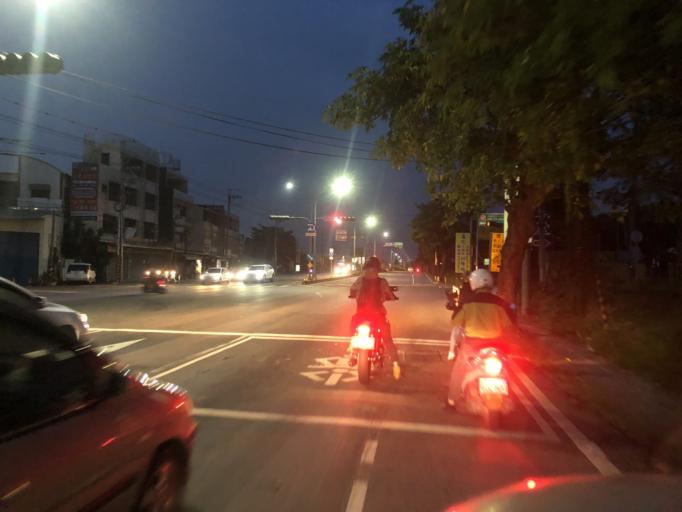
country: TW
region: Taiwan
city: Yujing
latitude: 23.1731
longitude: 120.3383
